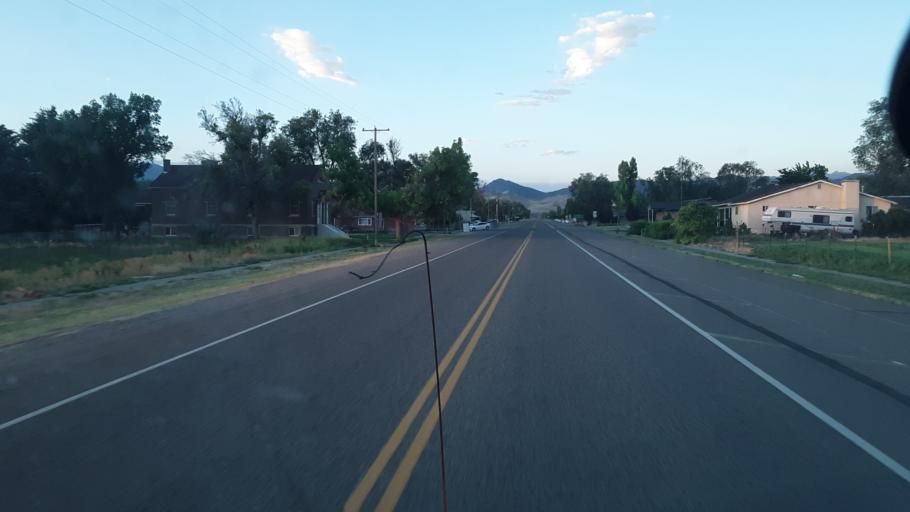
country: US
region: Utah
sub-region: Sevier County
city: Monroe
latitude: 38.6273
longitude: -112.2182
